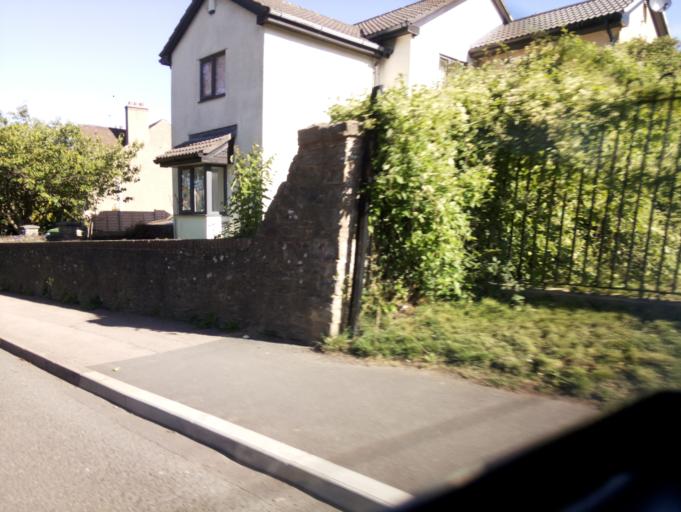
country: GB
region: England
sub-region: Gloucestershire
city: Coleford
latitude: 51.7925
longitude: -2.6101
